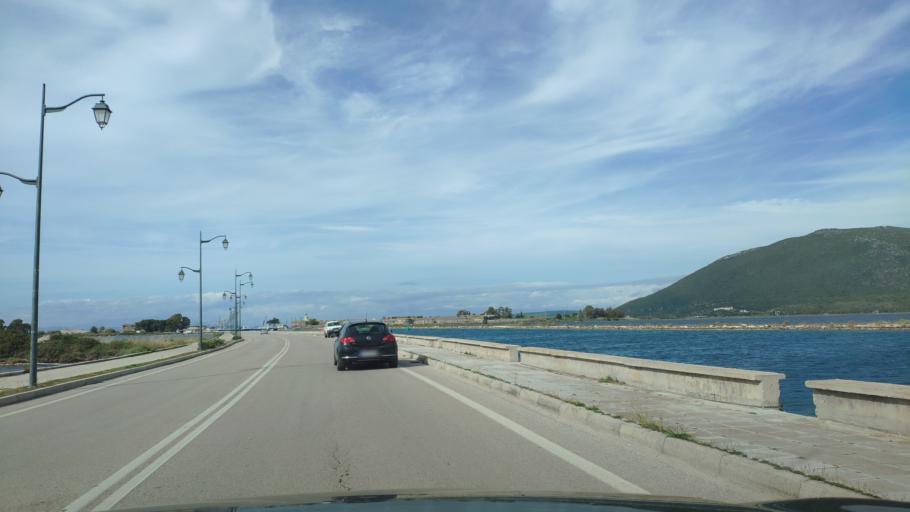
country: GR
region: Ionian Islands
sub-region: Lefkada
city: Lefkada
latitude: 38.8385
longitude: 20.7140
